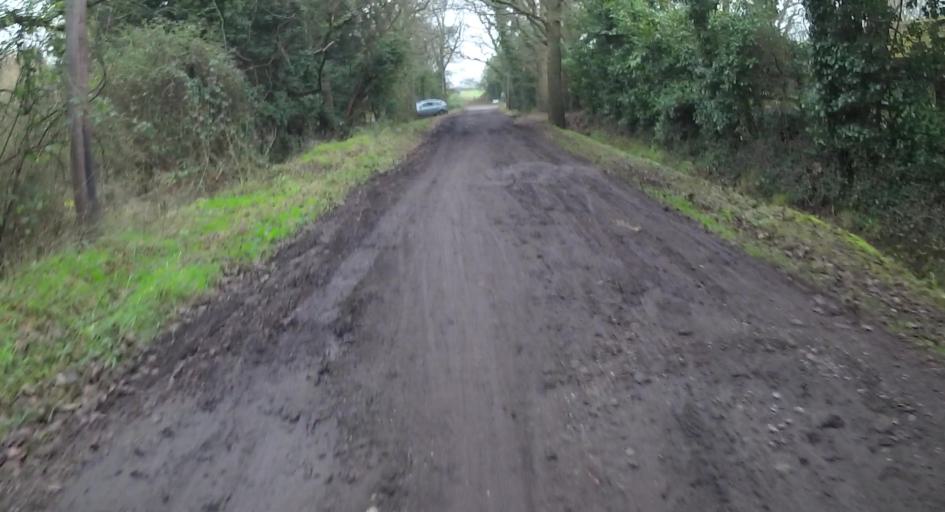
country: GB
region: England
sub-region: Wokingham
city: Barkham
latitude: 51.3934
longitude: -0.8601
